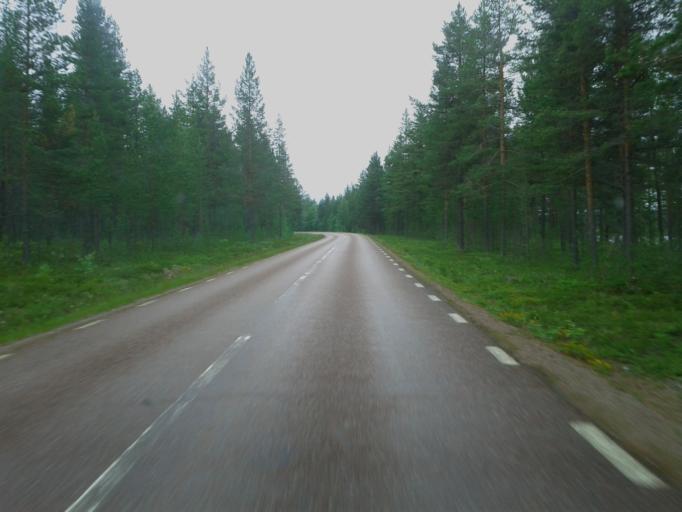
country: NO
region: Hedmark
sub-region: Trysil
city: Innbygda
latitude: 61.7880
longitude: 12.9298
